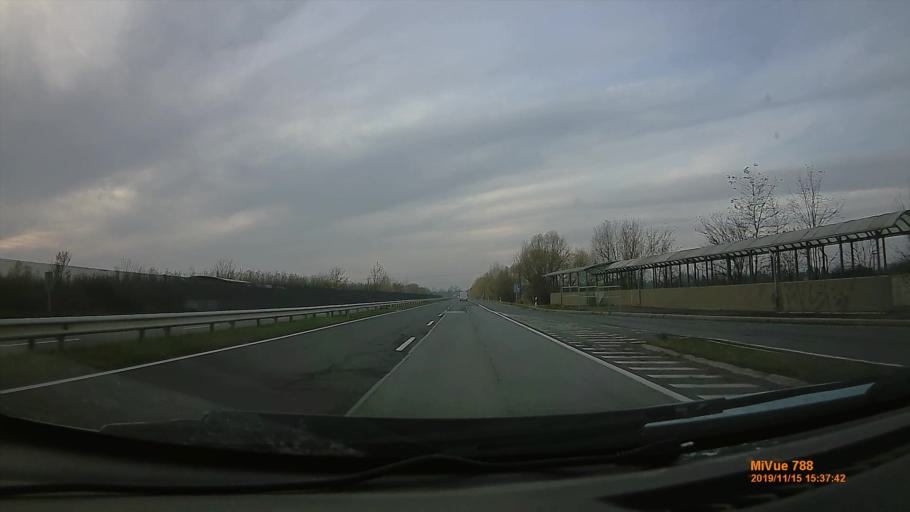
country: HU
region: Bekes
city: Doboz
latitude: 46.6661
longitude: 21.1940
